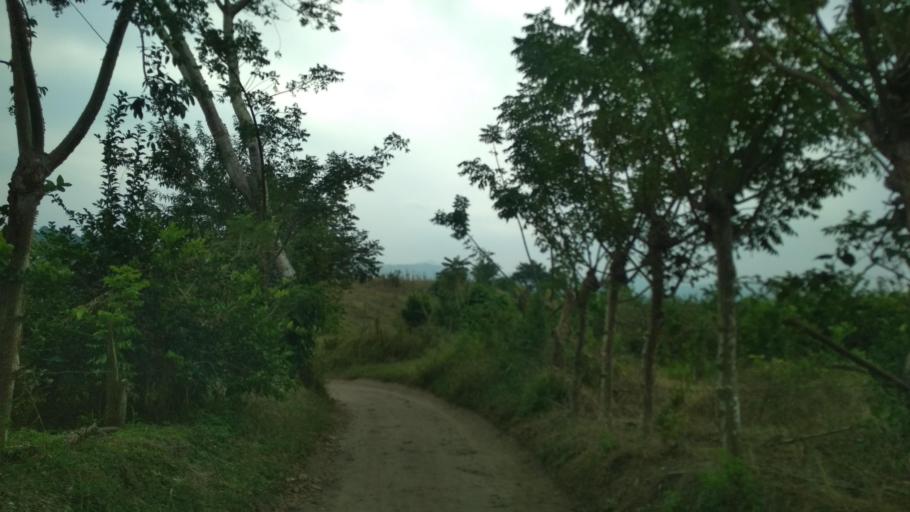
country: MM
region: Kayah
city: Loikaw
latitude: 20.2160
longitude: 97.3320
